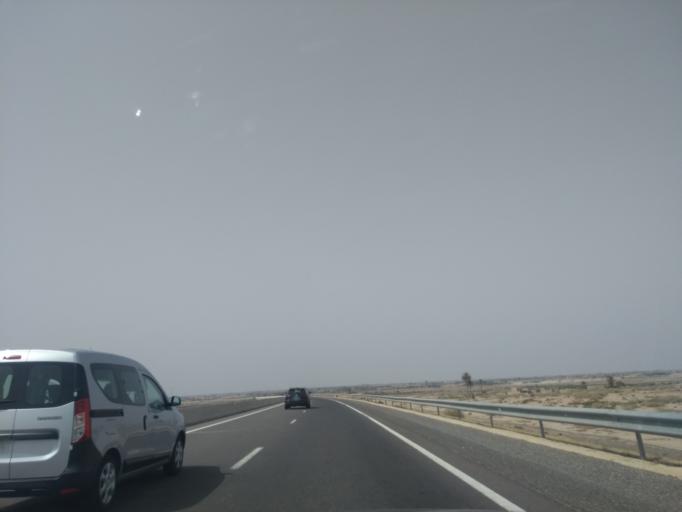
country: MA
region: Marrakech-Tensift-Al Haouz
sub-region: Marrakech
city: Marrakesh
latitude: 31.6685
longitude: -8.2903
